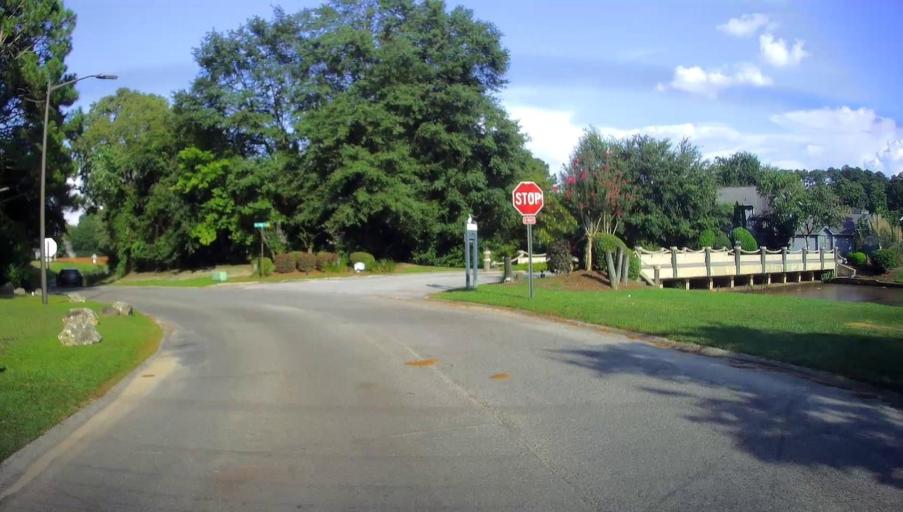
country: US
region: Georgia
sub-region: Houston County
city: Warner Robins
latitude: 32.5854
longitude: -83.6338
